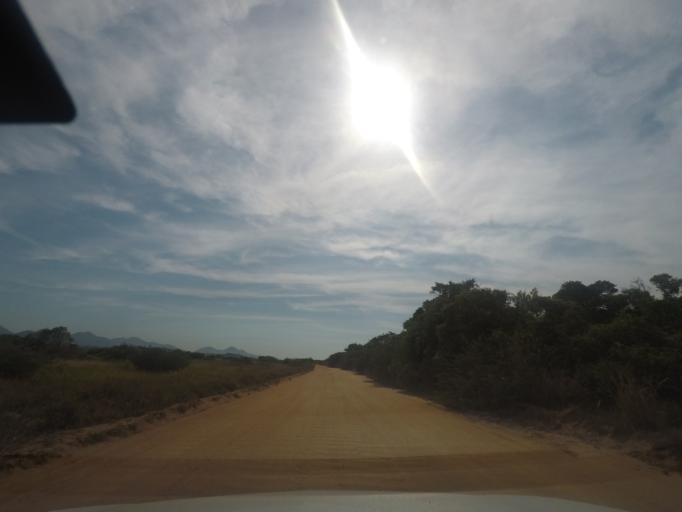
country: BR
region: Rio de Janeiro
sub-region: Marica
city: Marica
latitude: -22.9607
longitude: -42.8586
